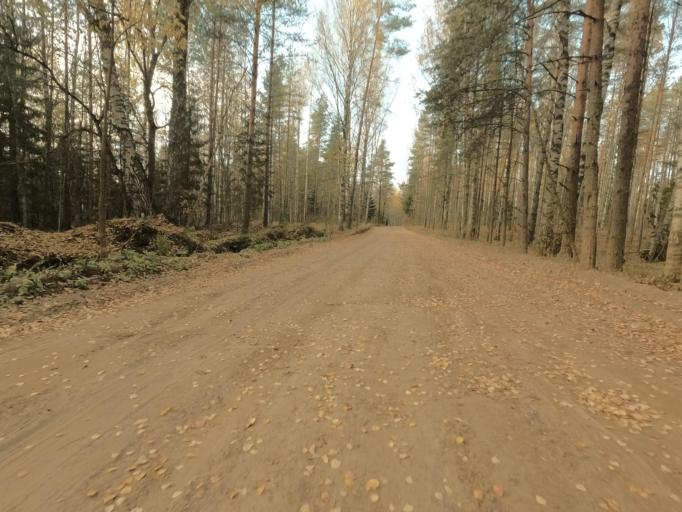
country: RU
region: Leningrad
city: Priladozhskiy
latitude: 59.7400
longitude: 31.3157
